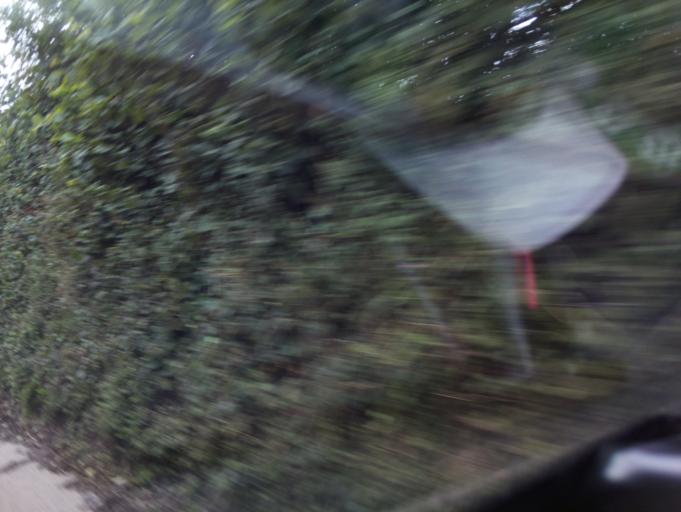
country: GB
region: England
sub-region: Devon
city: Kingsbridge
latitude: 50.2780
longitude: -3.8182
